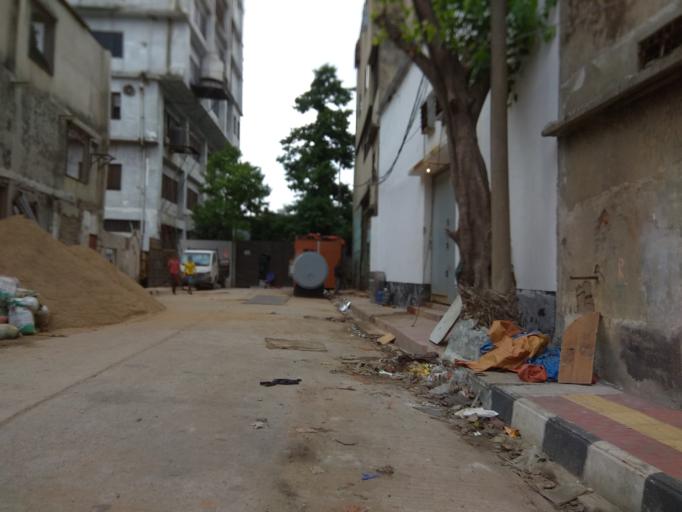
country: BD
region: Dhaka
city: Azimpur
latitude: 23.8113
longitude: 90.3578
